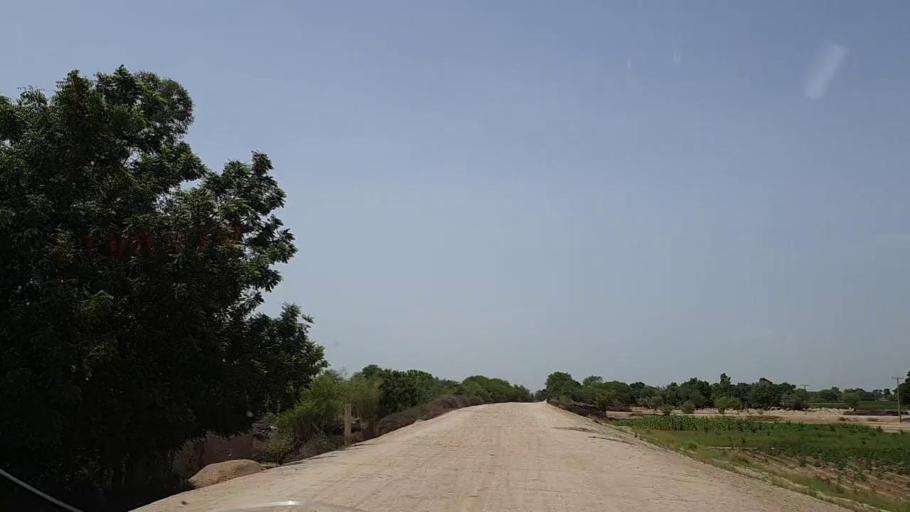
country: PK
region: Sindh
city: Tharu Shah
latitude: 27.0324
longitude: 68.1129
